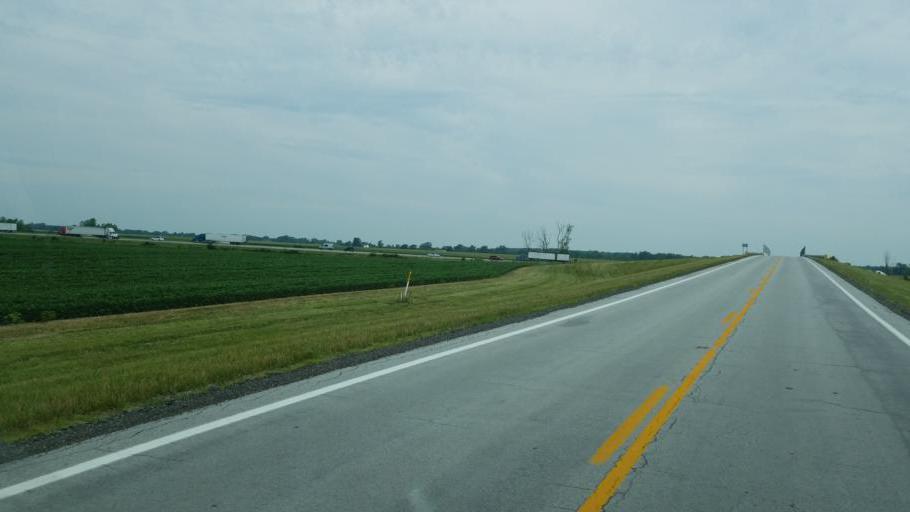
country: US
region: Ohio
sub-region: Madison County
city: Choctaw Lake
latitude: 39.9394
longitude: -83.4496
